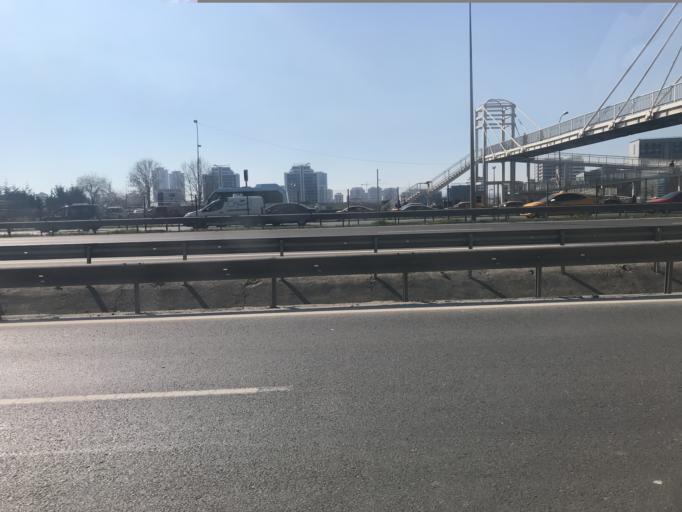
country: TR
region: Istanbul
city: Maltepe
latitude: 40.9159
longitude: 29.1825
